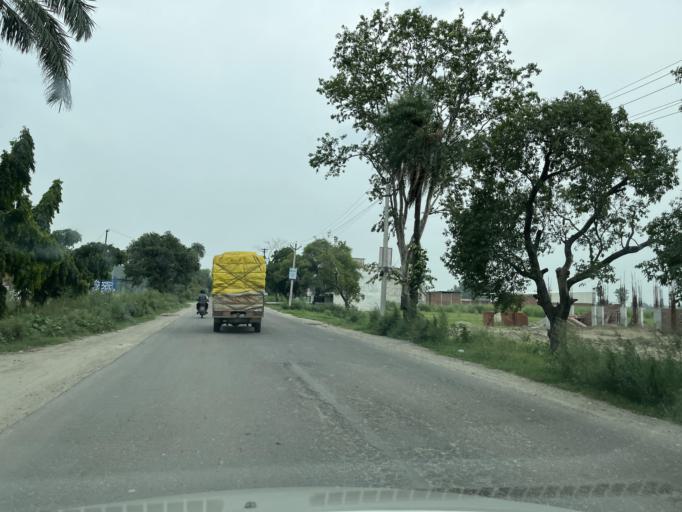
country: IN
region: Uttar Pradesh
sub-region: Rampur
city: Bilaspur
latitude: 29.0351
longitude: 79.2571
